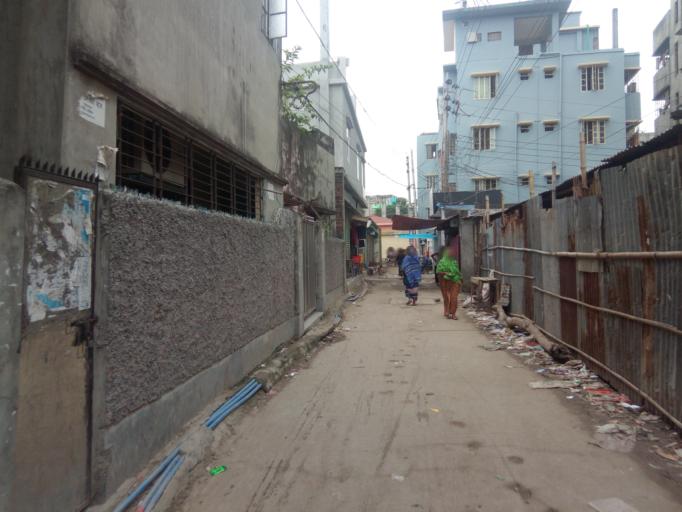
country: BD
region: Dhaka
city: Paltan
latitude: 23.7539
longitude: 90.4349
